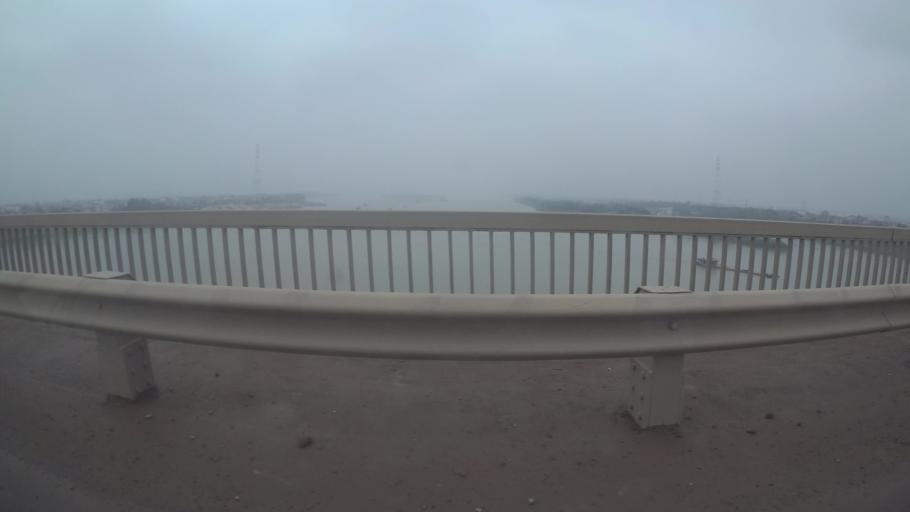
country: VN
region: Ha Noi
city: Tay Ho
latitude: 21.0978
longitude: 105.7863
